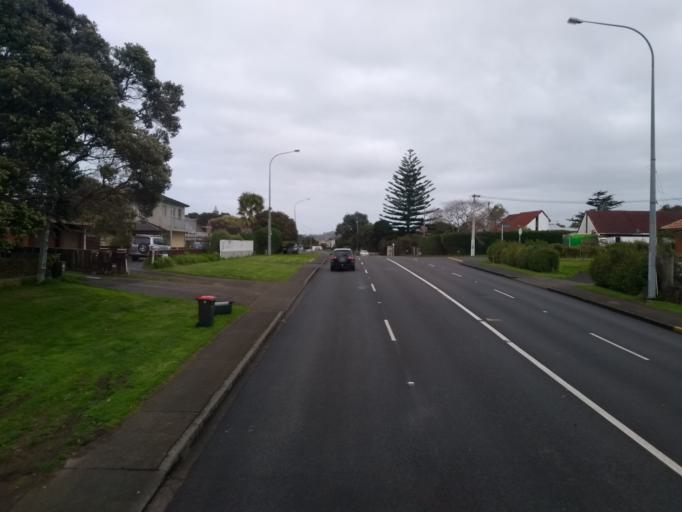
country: NZ
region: Auckland
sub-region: Auckland
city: Tamaki
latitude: -36.8963
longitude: 174.8372
